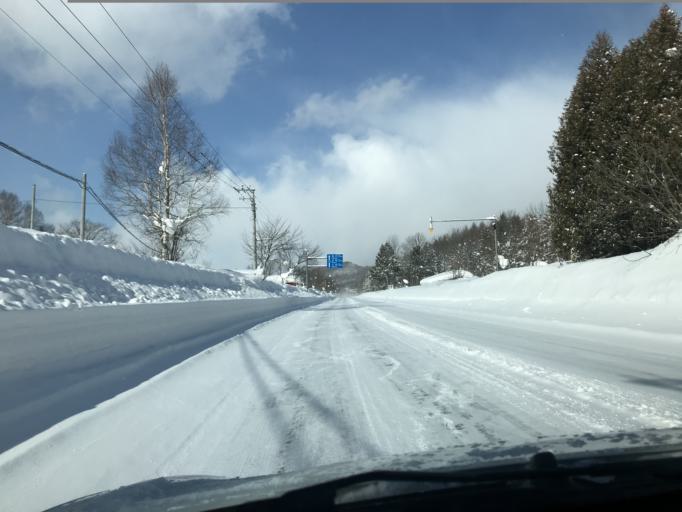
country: JP
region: Hokkaido
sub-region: Asahikawa-shi
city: Asahikawa
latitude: 43.9277
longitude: 142.4737
